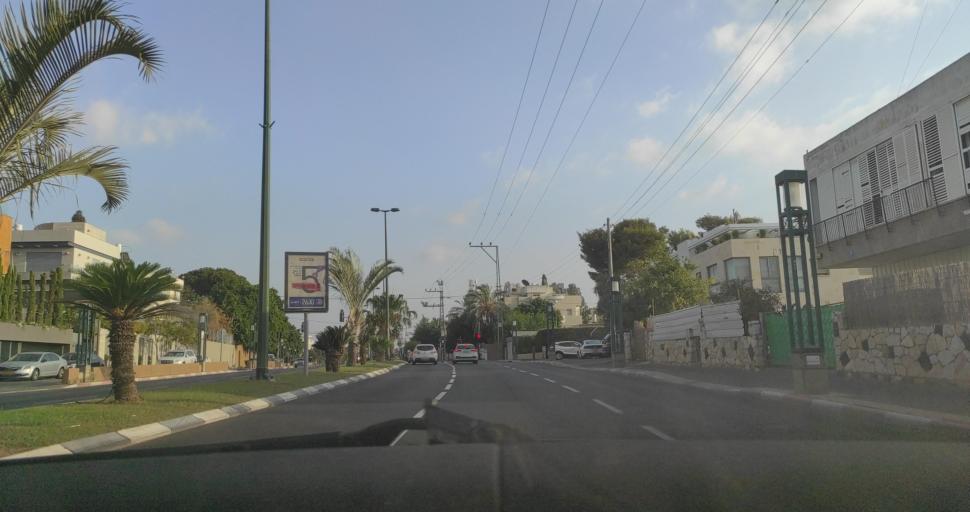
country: IL
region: Tel Aviv
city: Bene Beraq
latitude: 32.1113
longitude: 34.8252
